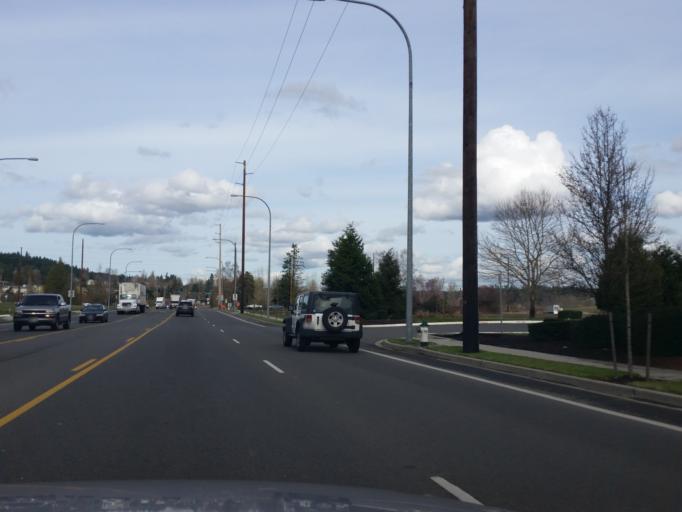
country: US
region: Washington
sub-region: Pierce County
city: Fife
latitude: 47.2366
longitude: -122.3363
